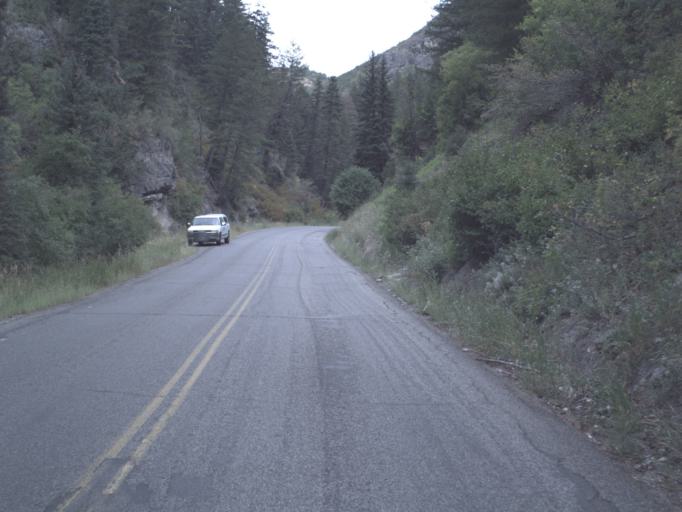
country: US
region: Utah
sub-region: Utah County
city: Orem
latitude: 40.3874
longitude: -111.5739
